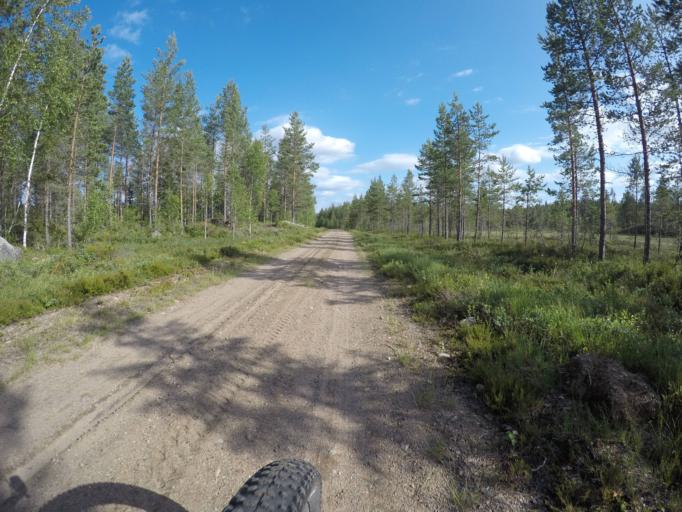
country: SE
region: OErebro
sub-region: Hallefors Kommun
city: Haellefors
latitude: 60.0727
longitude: 14.5141
